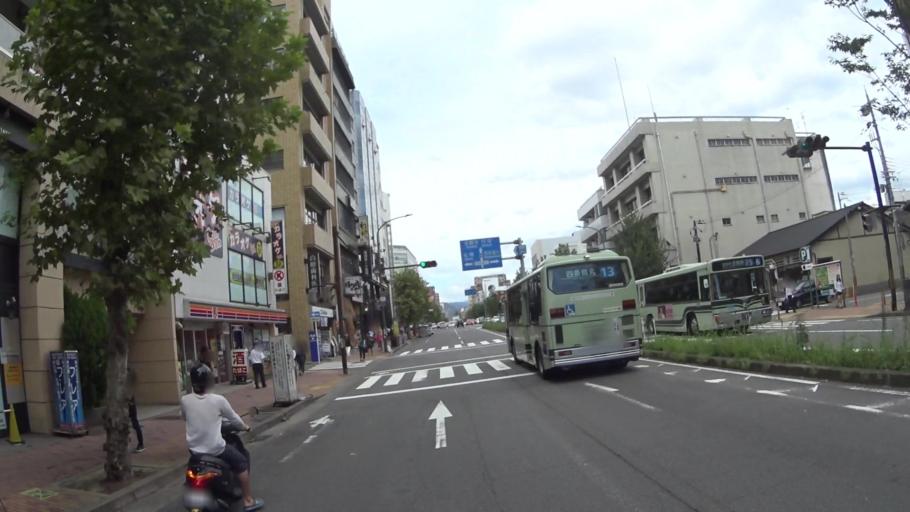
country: JP
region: Kyoto
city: Kyoto
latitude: 35.0019
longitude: 135.7320
